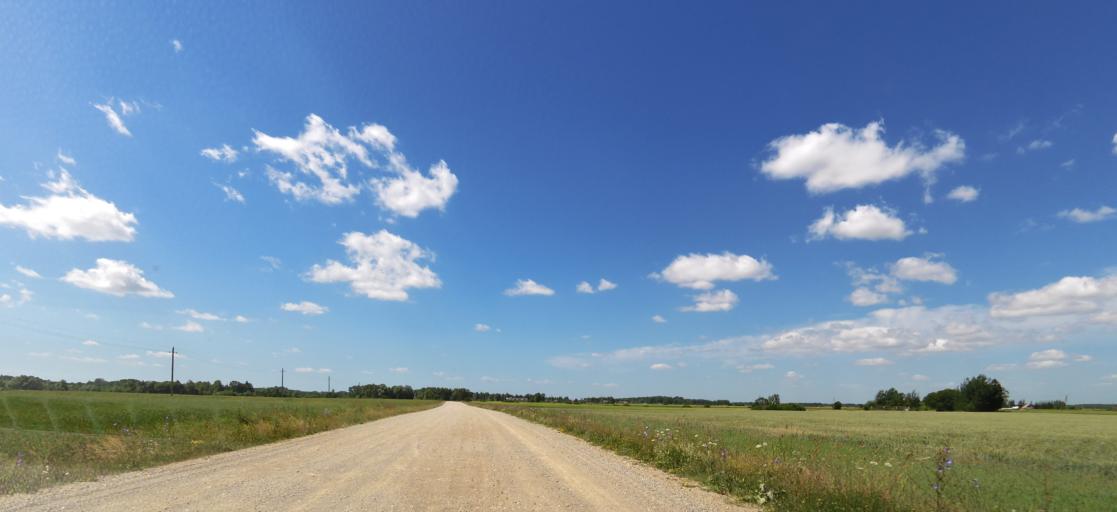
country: LT
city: Kupiskis
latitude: 55.9399
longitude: 24.9609
